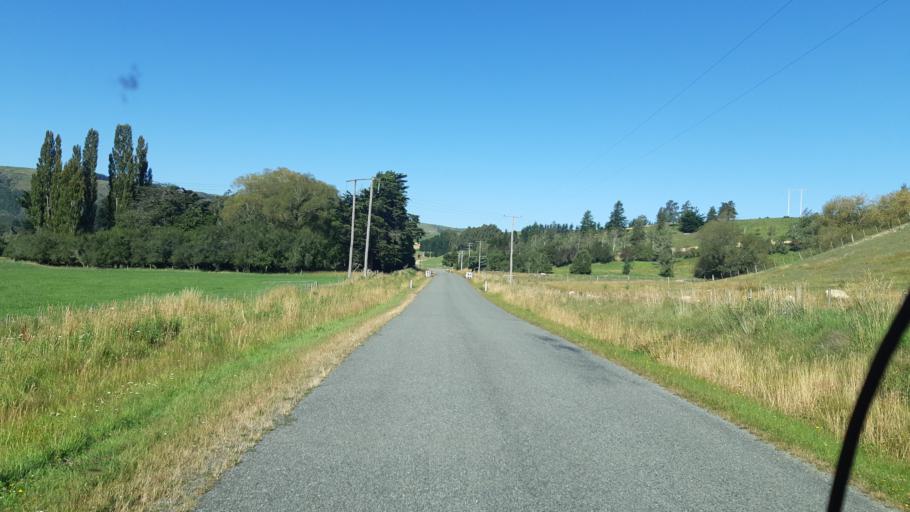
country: NZ
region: Canterbury
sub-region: Timaru District
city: Pleasant Point
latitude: -44.2884
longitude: 170.8902
